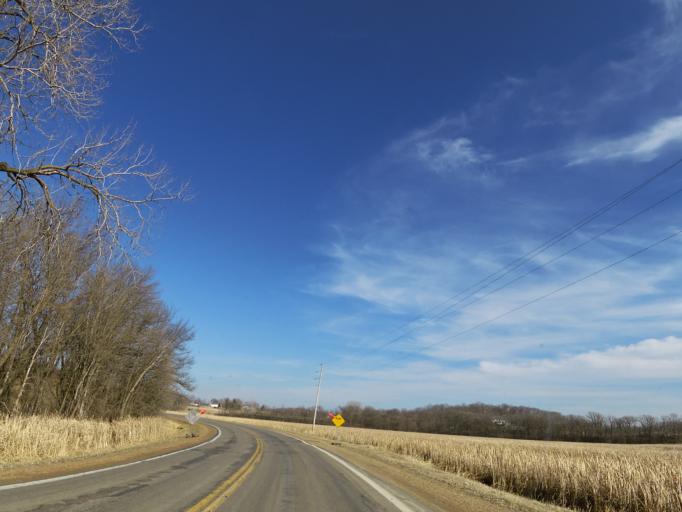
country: US
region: Minnesota
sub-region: Scott County
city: Prior Lake
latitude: 44.6306
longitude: -93.4500
